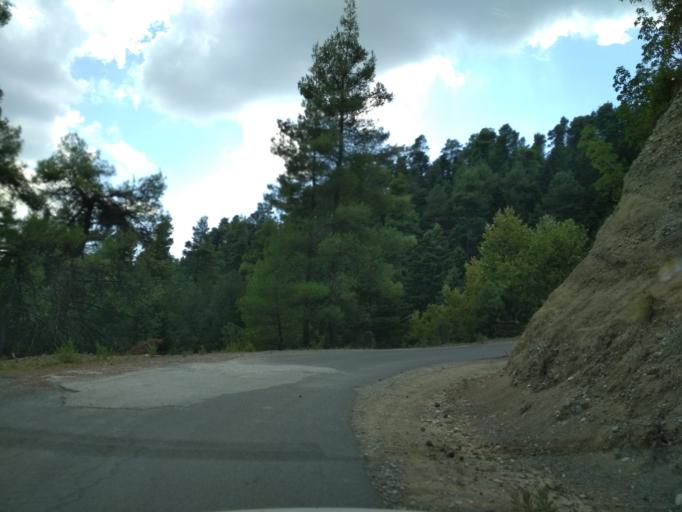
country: GR
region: Central Greece
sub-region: Nomos Evvoias
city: Roviai
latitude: 38.8592
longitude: 23.2853
